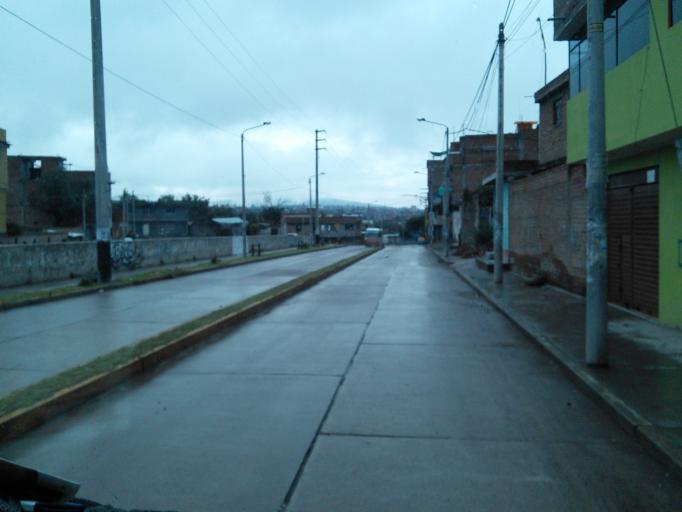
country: PE
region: Ayacucho
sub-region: Provincia de Huamanga
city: Ayacucho
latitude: -13.1678
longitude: -74.2259
